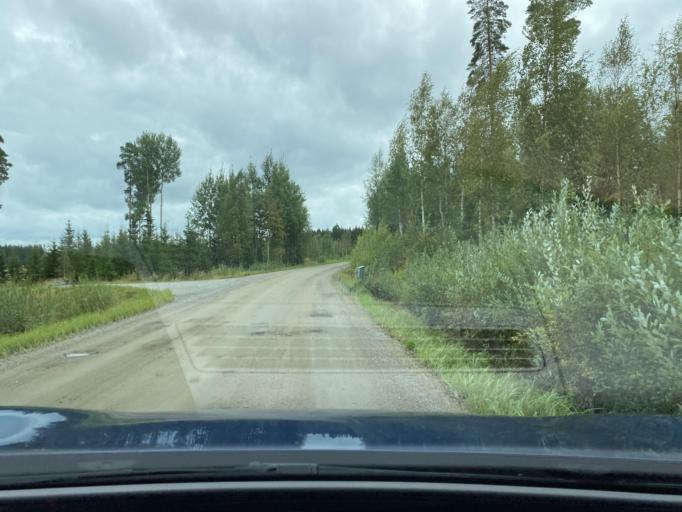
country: FI
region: Pirkanmaa
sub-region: Lounais-Pirkanmaa
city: Punkalaidun
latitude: 61.2206
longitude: 23.1632
